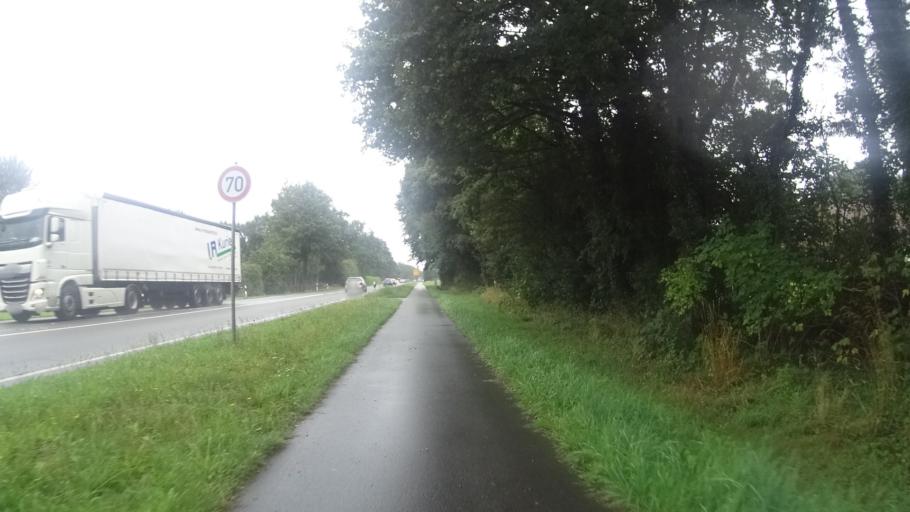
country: DE
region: Lower Saxony
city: Holtland
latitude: 53.2924
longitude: 7.5861
